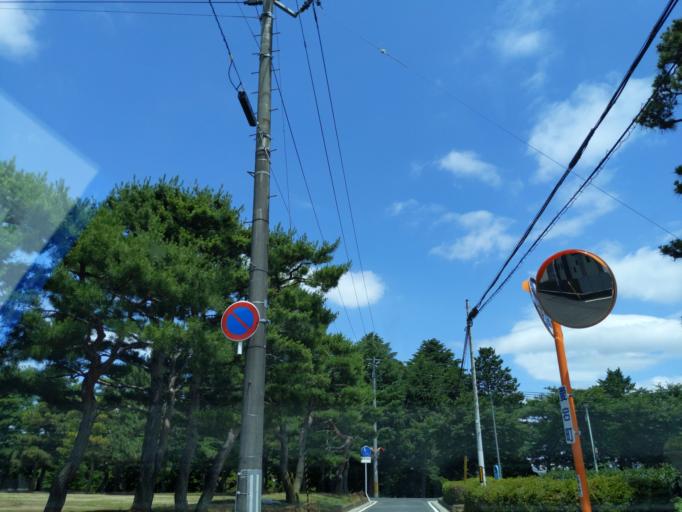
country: JP
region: Fukushima
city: Koriyama
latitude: 37.3892
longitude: 140.3761
